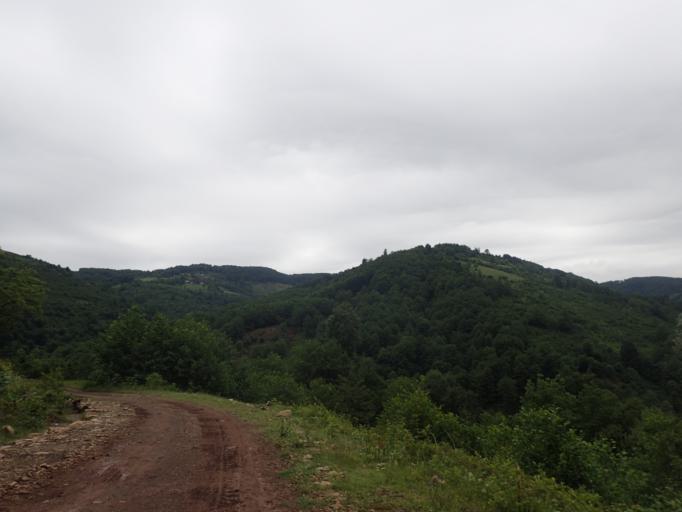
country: TR
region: Ordu
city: Akkus
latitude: 40.9357
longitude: 36.9253
